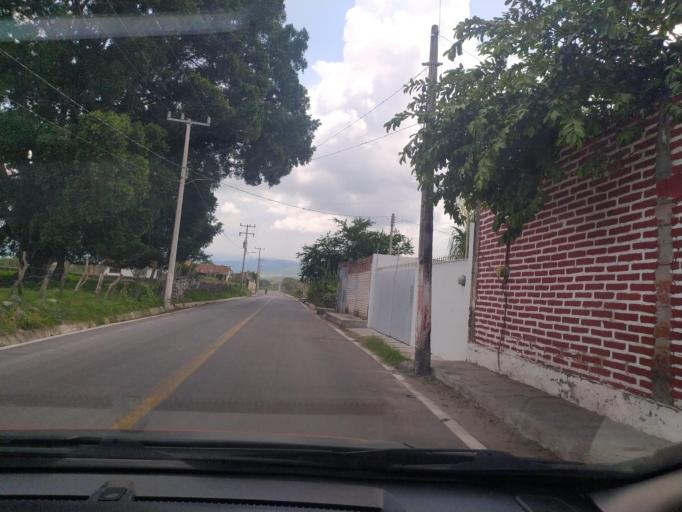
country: MX
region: Jalisco
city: Villa Corona
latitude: 20.3534
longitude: -103.6672
